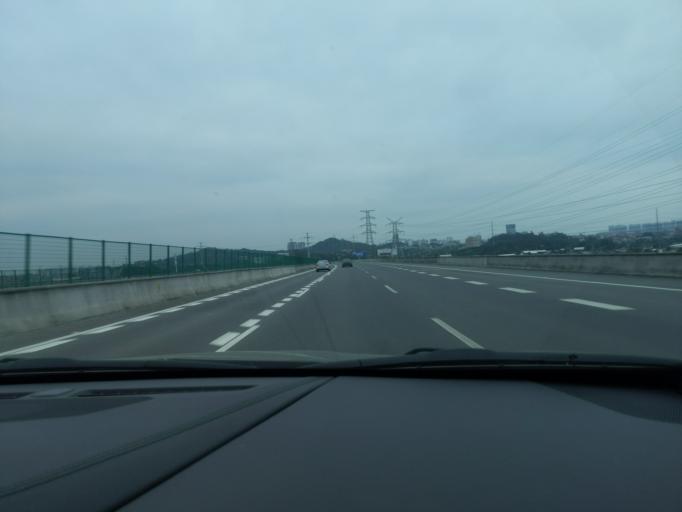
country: CN
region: Fujian
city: Shishi
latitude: 24.7496
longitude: 118.5828
